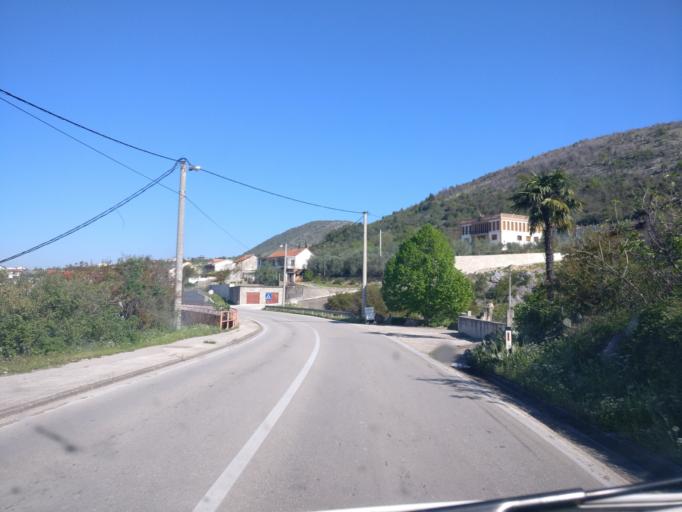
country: BA
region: Federation of Bosnia and Herzegovina
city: Capljina
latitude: 43.1376
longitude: 17.6707
